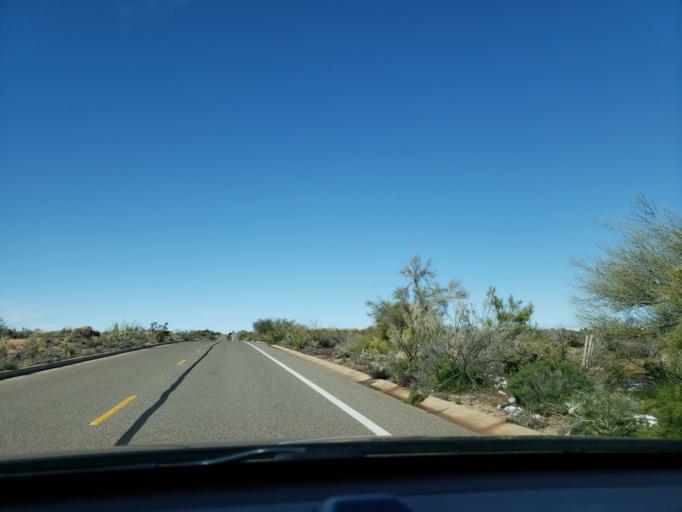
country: US
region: Arizona
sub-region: Maricopa County
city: Carefree
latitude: 33.7204
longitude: -111.8264
